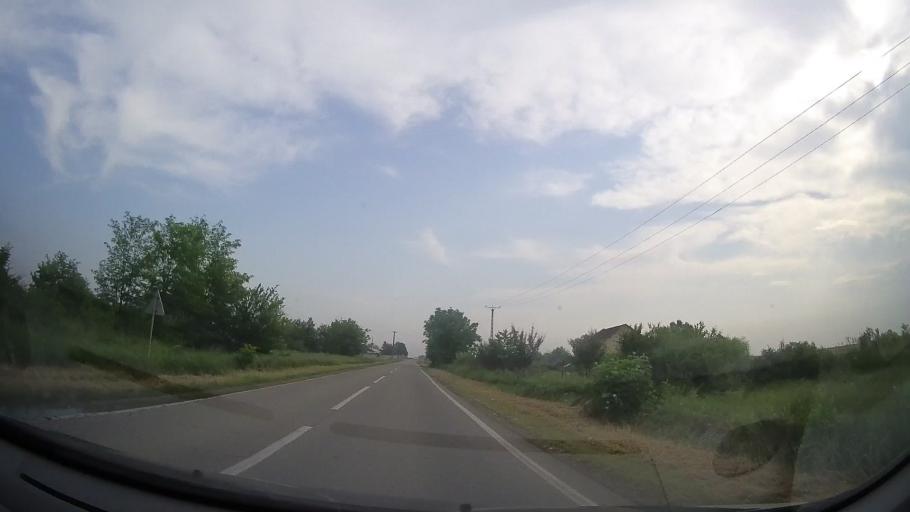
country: RO
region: Timis
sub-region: Comuna Sag
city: Sag
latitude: 45.6606
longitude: 21.1494
